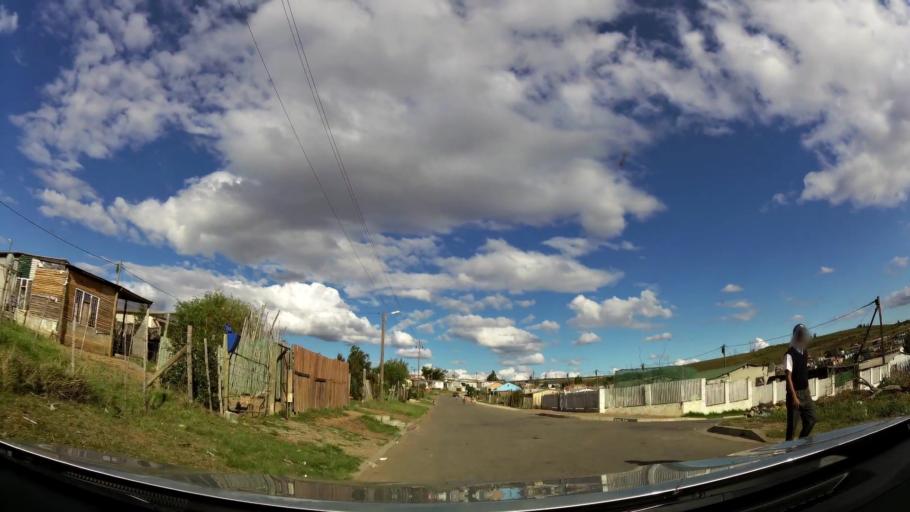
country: ZA
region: Western Cape
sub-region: Overberg District Municipality
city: Swellendam
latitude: -34.0332
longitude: 20.4511
